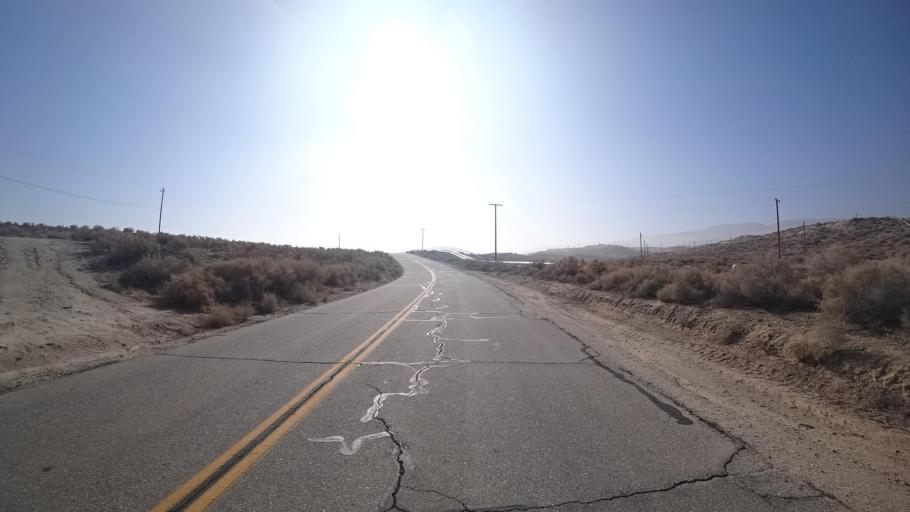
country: US
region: California
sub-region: Kern County
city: Taft Heights
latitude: 35.1483
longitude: -119.5146
